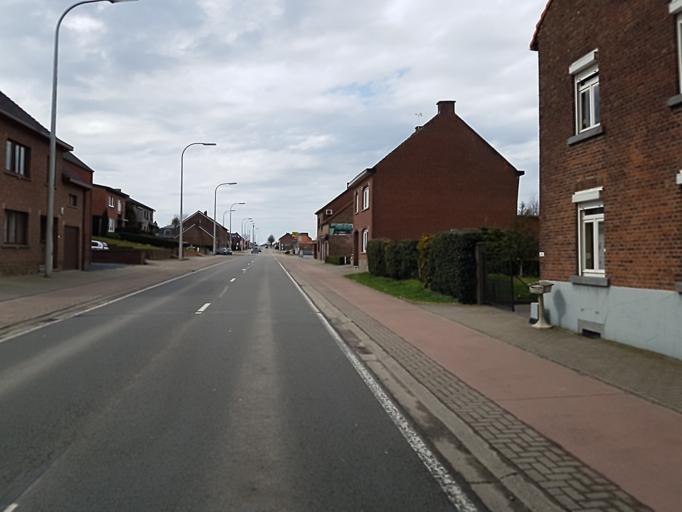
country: BE
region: Flanders
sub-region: Provincie Limburg
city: Borgloon
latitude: 50.7870
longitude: 5.3978
